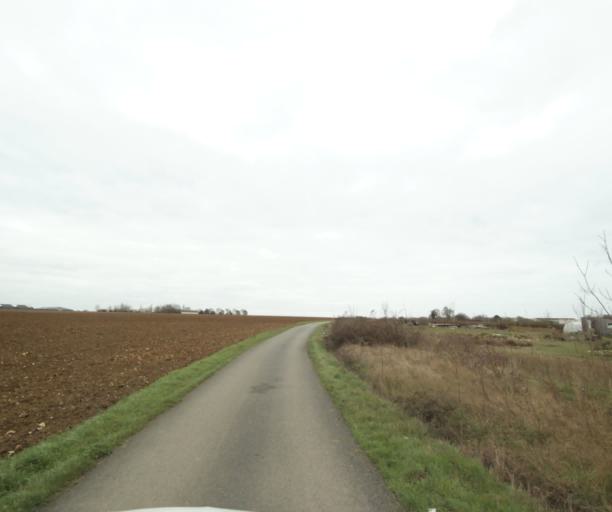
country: FR
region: Poitou-Charentes
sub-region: Departement de la Charente-Maritime
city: Nieul-sur-Mer
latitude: 46.1961
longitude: -1.1663
